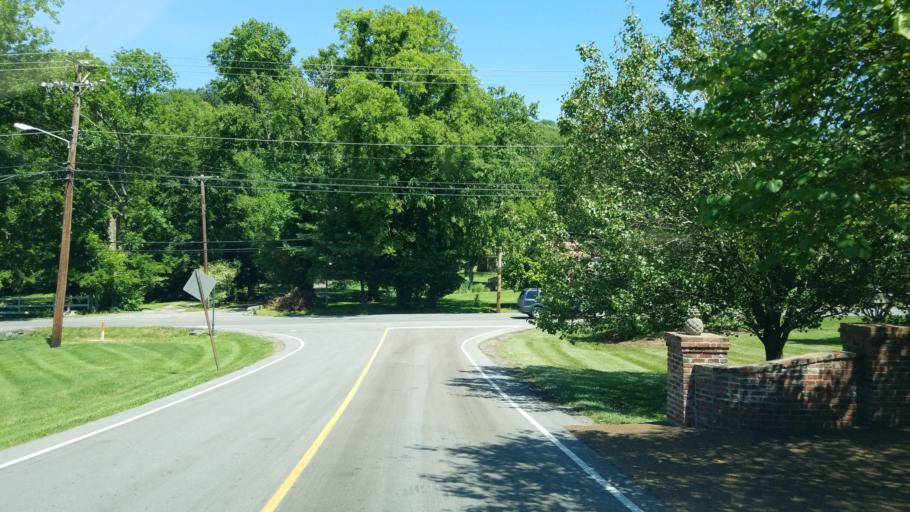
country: US
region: Tennessee
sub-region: Davidson County
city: Forest Hills
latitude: 36.0611
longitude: -86.8150
